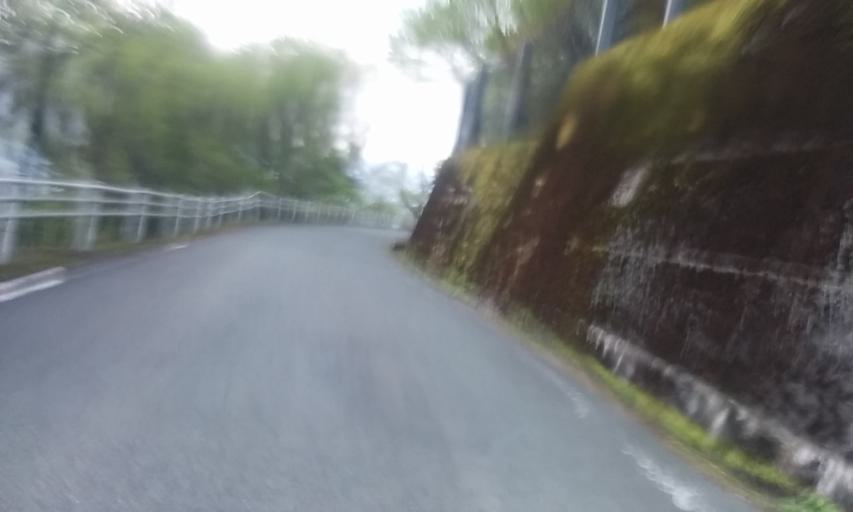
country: JP
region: Ehime
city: Saijo
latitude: 33.7976
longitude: 133.2658
